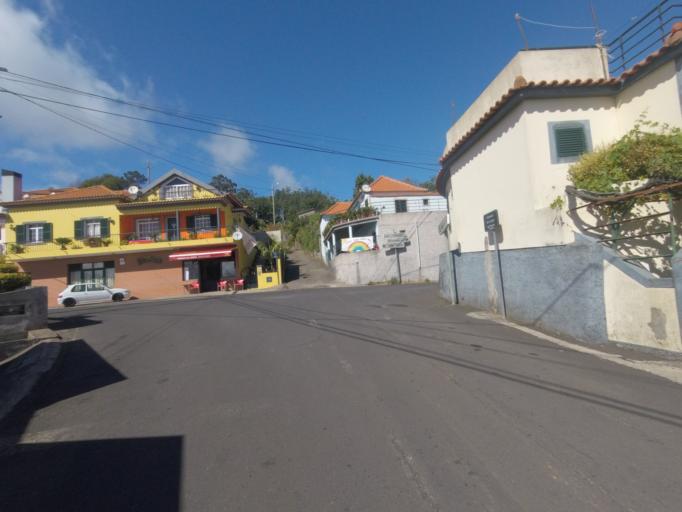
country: PT
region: Madeira
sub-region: Ribeira Brava
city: Campanario
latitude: 32.6953
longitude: -17.0172
